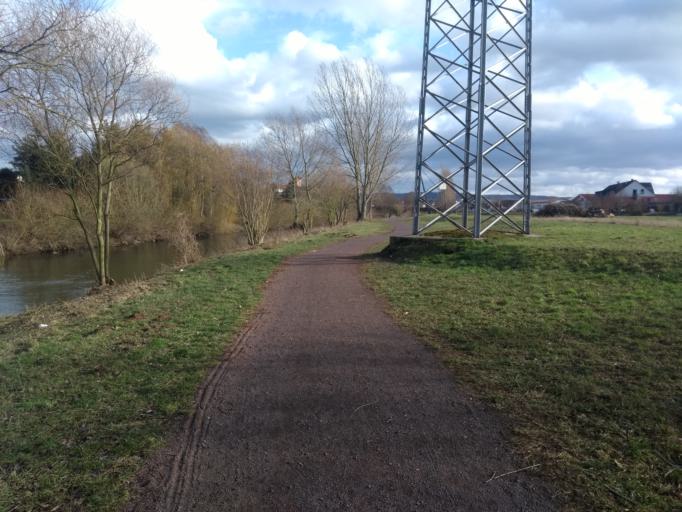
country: DE
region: Thuringia
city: Breitungen
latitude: 50.7605
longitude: 10.3297
